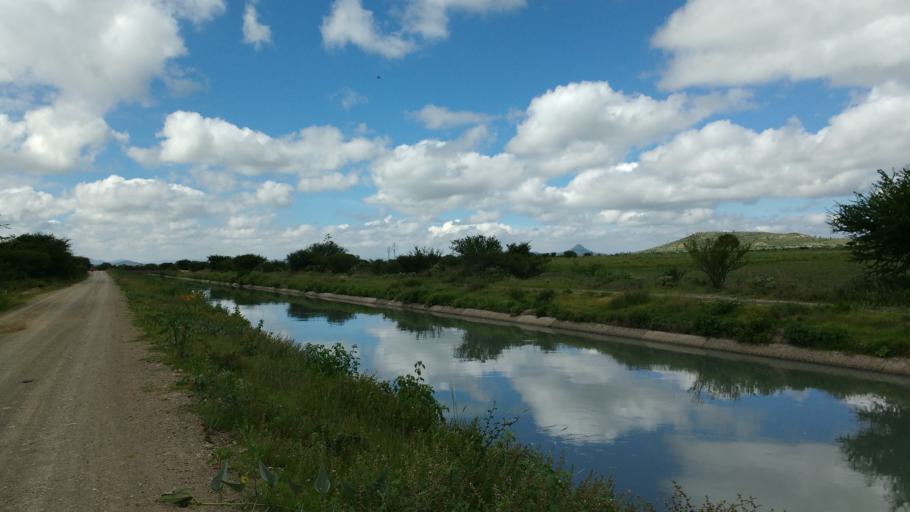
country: MX
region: Hidalgo
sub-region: Tezontepec de Aldama
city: Tenango
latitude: 20.2509
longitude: -99.2541
